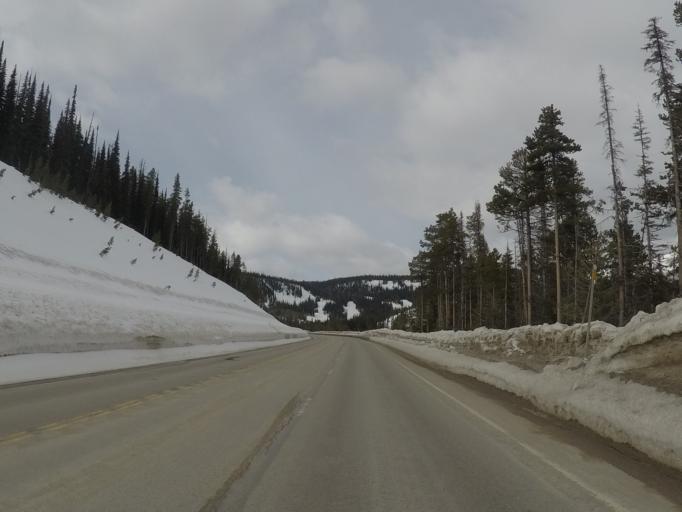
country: US
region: Idaho
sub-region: Lemhi County
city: Salmon
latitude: 45.7006
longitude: -113.9430
